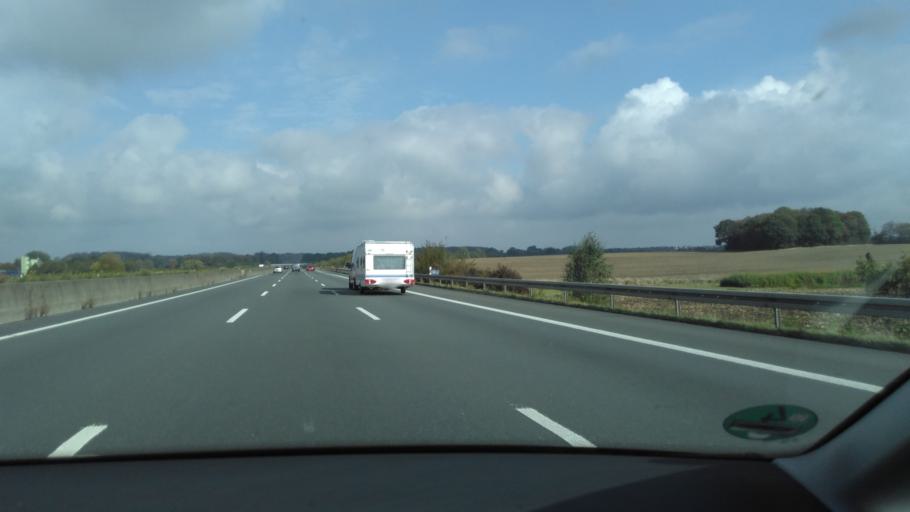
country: DE
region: North Rhine-Westphalia
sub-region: Regierungsbezirk Munster
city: Beckum
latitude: 51.7508
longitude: 7.9962
